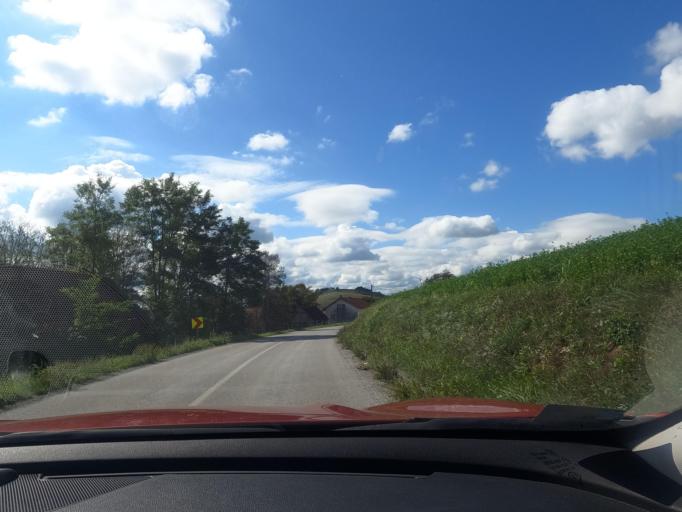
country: BA
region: Federation of Bosnia and Herzegovina
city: Velika Kladusa
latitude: 45.2117
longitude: 15.8208
